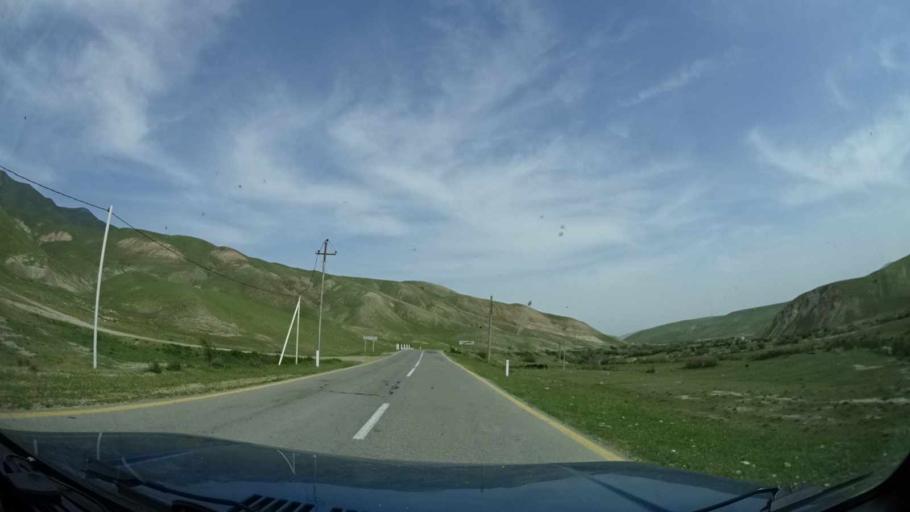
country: AZ
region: Xizi
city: Khyzy
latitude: 40.8854
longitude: 49.1732
